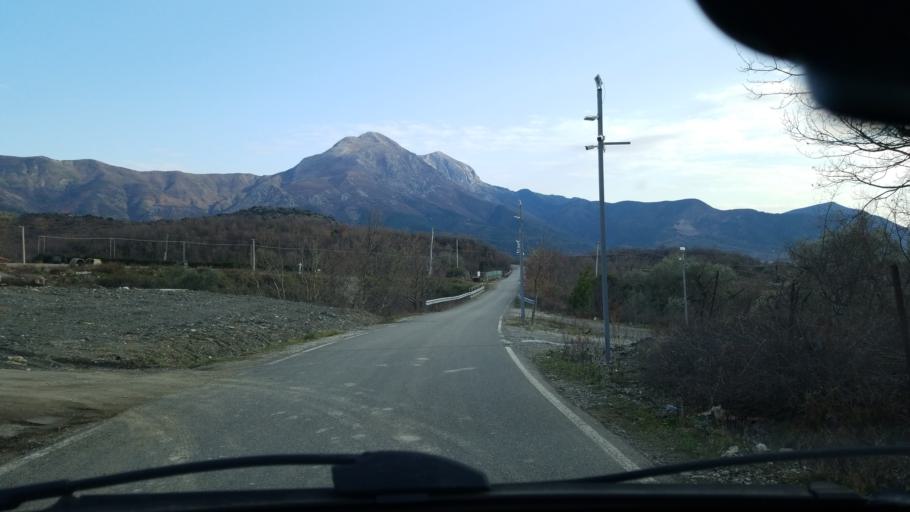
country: AL
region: Lezhe
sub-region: Rrethi i Lezhes
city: Kallmeti i Madh
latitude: 41.8816
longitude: 19.6919
